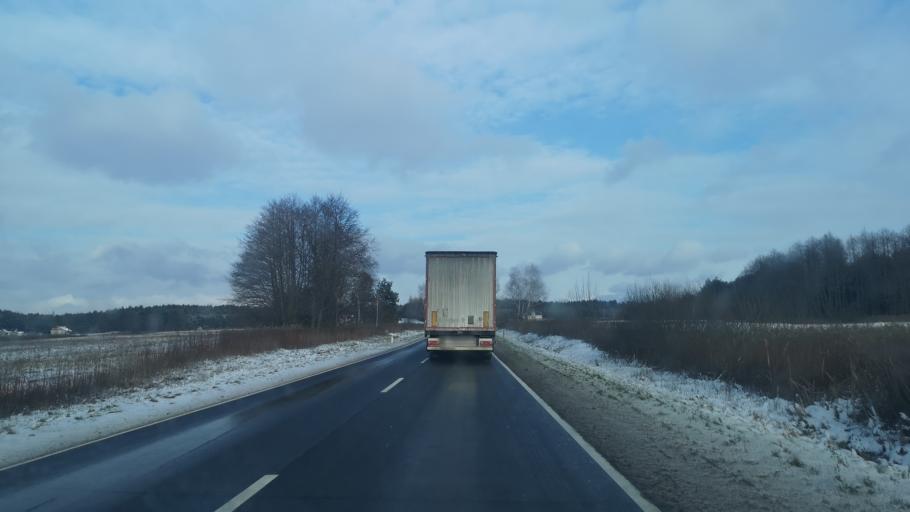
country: PL
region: Subcarpathian Voivodeship
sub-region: Powiat przeworski
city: Sieniawa
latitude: 50.2003
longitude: 22.6318
